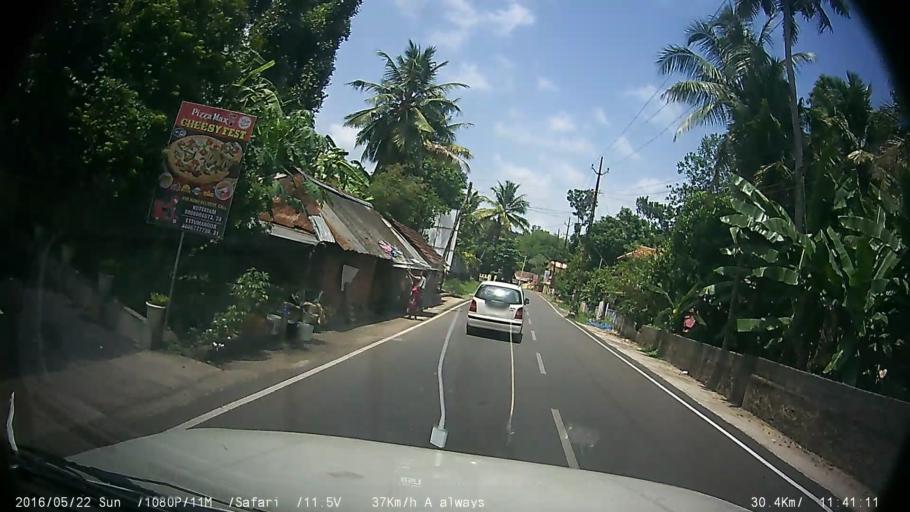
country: IN
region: Kerala
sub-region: Kottayam
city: Kottayam
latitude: 9.5499
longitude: 76.5188
